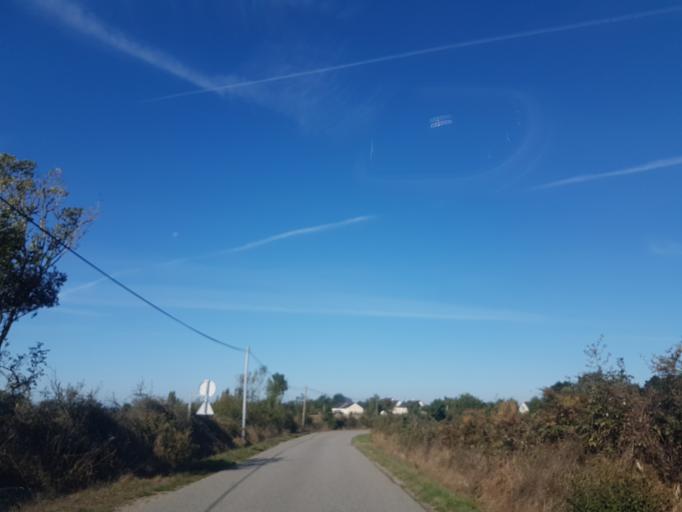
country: FR
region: Pays de la Loire
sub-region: Departement de la Loire-Atlantique
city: Petit-Mars
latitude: 47.3884
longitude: -1.4366
